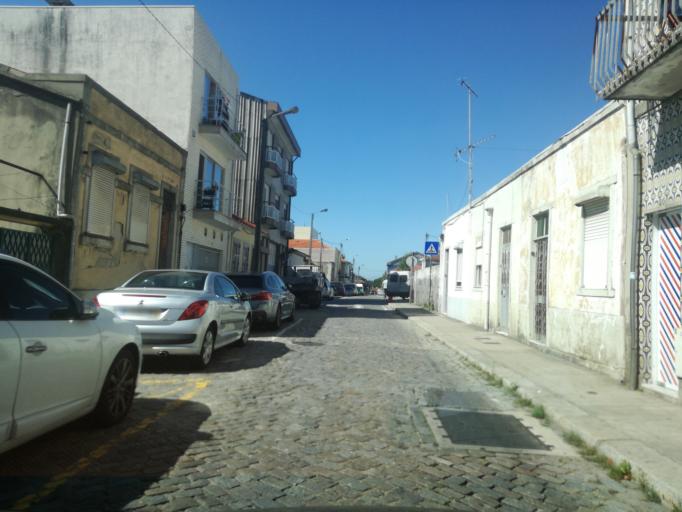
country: PT
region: Porto
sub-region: Matosinhos
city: Sao Mamede de Infesta
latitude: 41.1831
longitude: -8.5969
